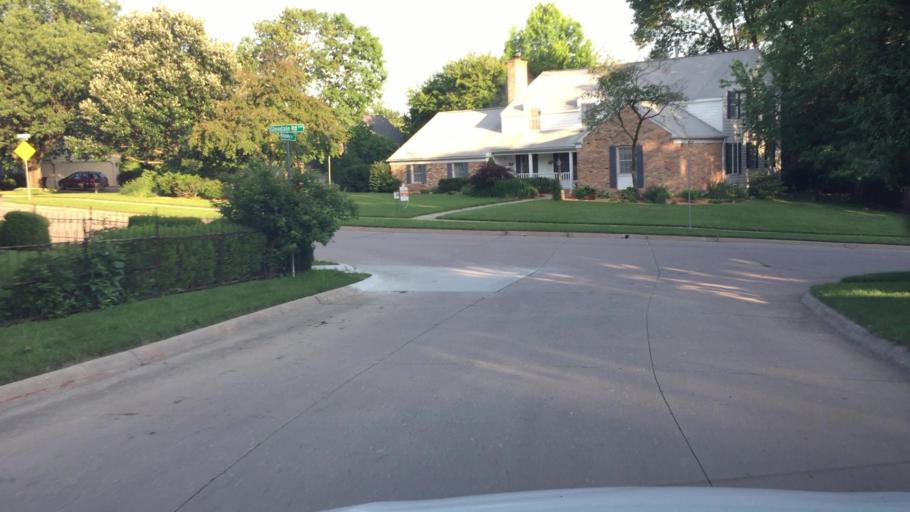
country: US
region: Iowa
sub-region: Johnson County
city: Iowa City
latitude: 41.6620
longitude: -91.5046
